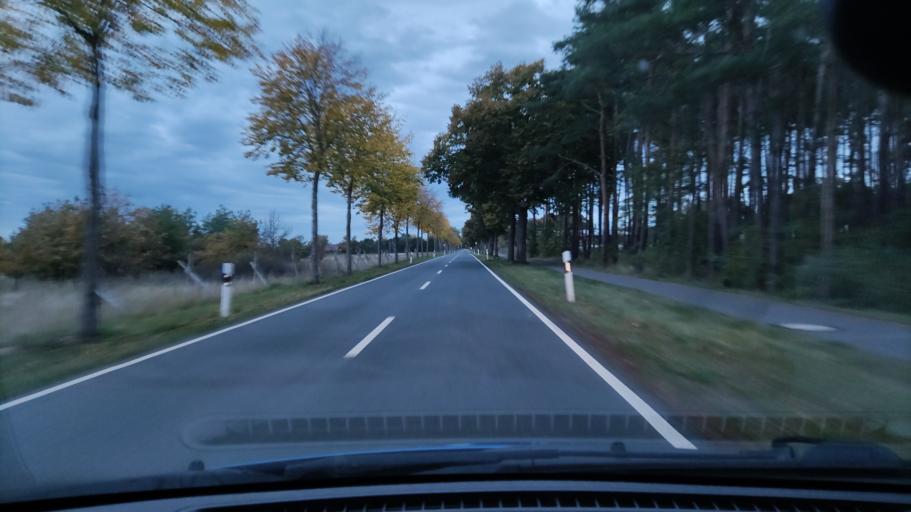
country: DE
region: Lower Saxony
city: Gorleben
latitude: 53.0619
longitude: 11.3978
